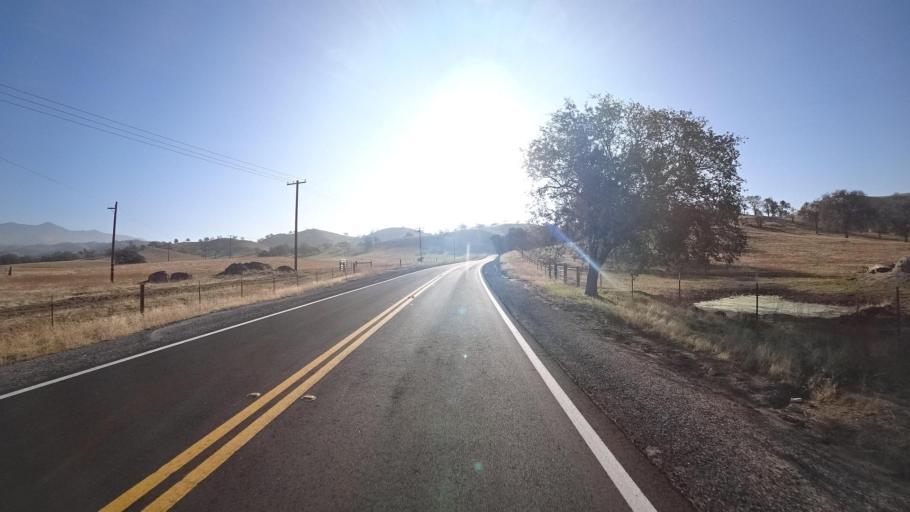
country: US
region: California
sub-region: Tulare County
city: Richgrove
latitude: 35.7305
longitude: -118.8587
